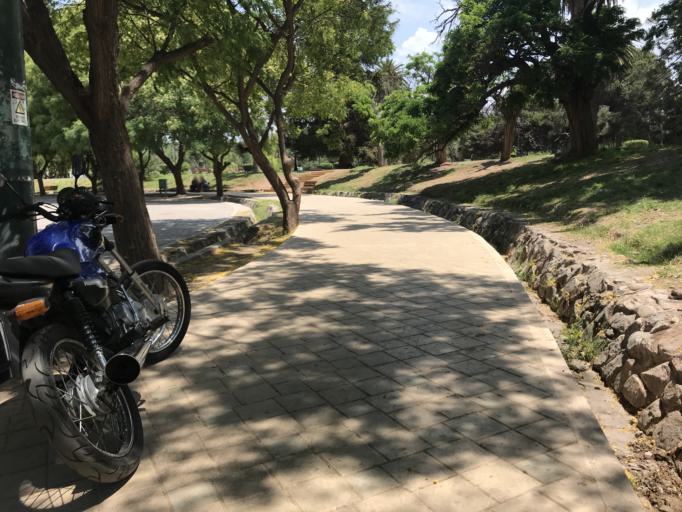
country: AR
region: Mendoza
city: Mendoza
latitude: -32.8899
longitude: -68.8664
